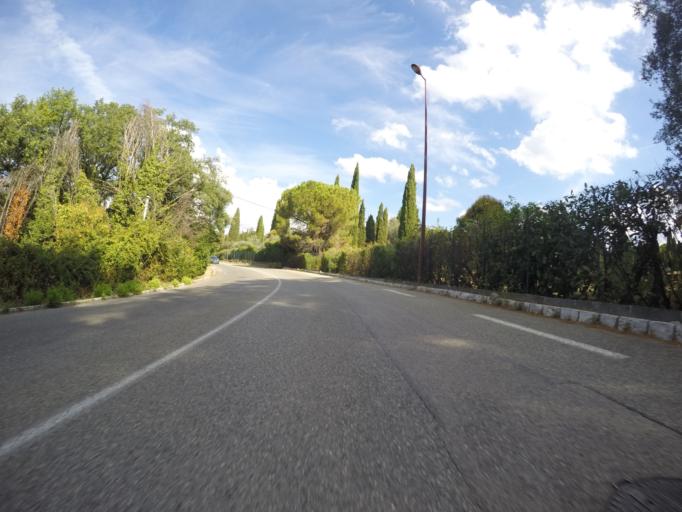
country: FR
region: Provence-Alpes-Cote d'Azur
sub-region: Departement des Alpes-Maritimes
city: Le Rouret
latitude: 43.6745
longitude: 7.0236
